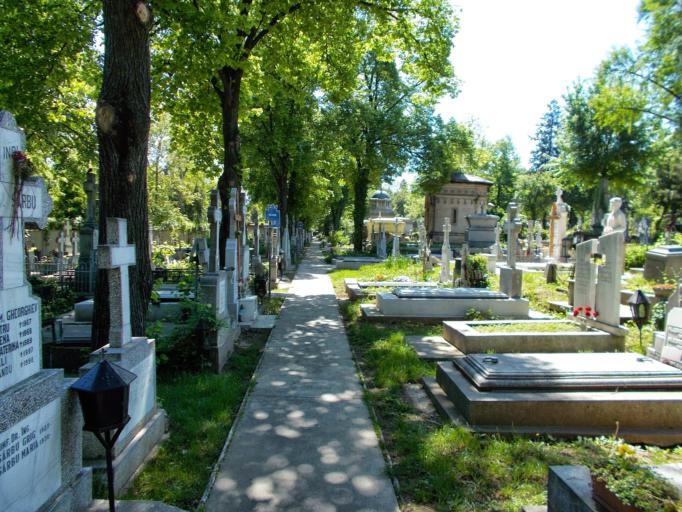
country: RO
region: Bucuresti
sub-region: Municipiul Bucuresti
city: Bucuresti
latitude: 44.4049
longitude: 26.1007
